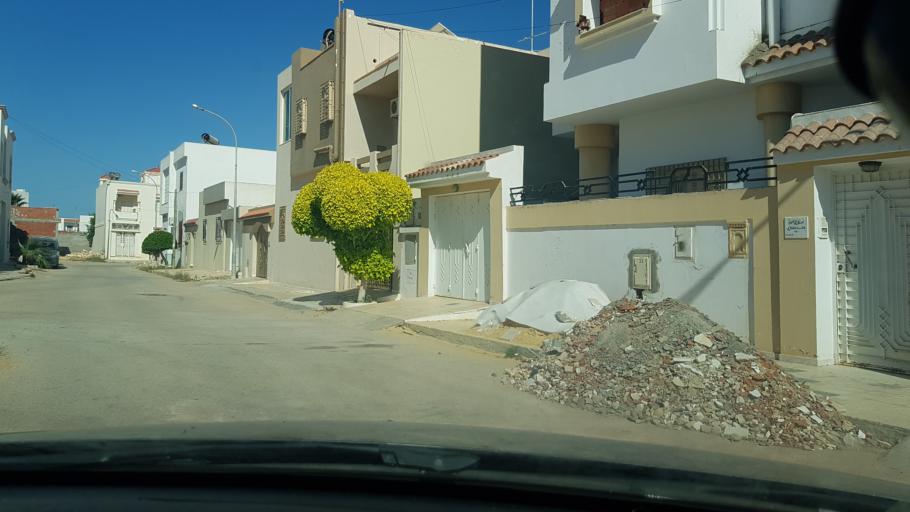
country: TN
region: Safaqis
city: Al Qarmadah
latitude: 34.8258
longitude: 10.7577
